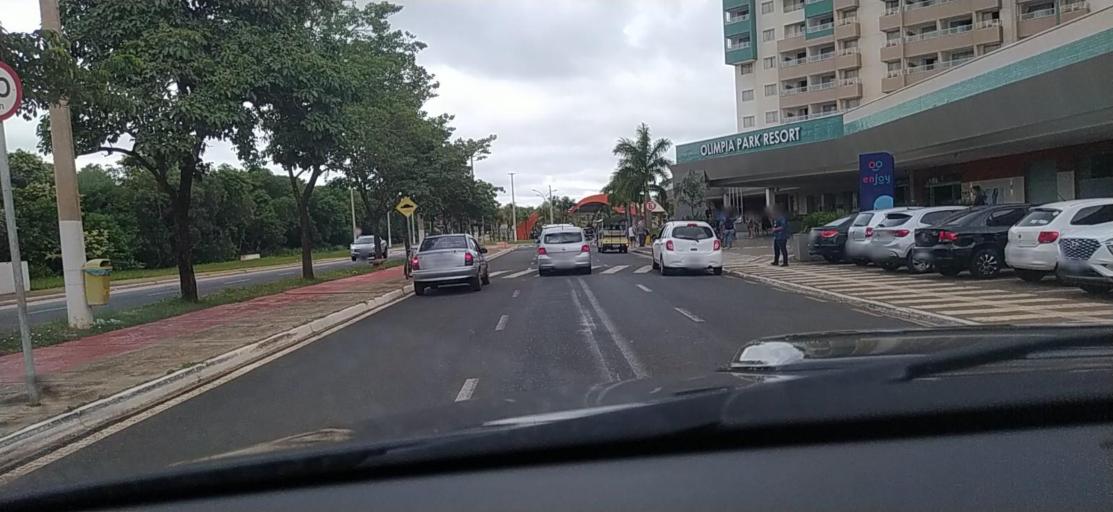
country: BR
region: Sao Paulo
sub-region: Olimpia
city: Olimpia
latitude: -20.7265
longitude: -48.9160
